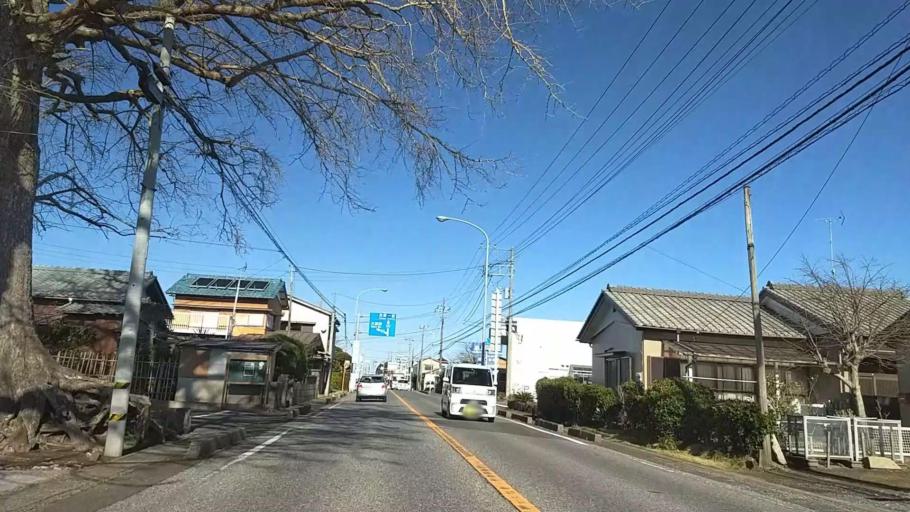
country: JP
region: Chiba
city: Ohara
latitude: 35.2353
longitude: 140.3892
